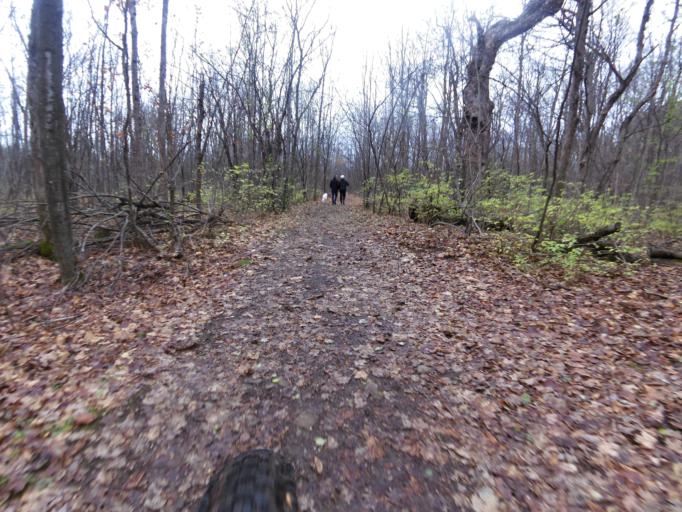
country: CA
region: Ontario
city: Bells Corners
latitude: 45.3107
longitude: -75.8166
